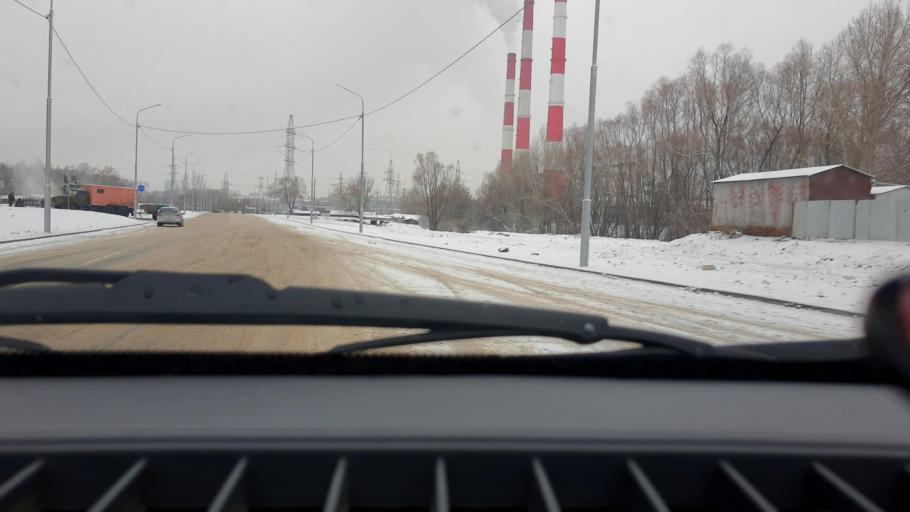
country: RU
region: Bashkortostan
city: Ufa
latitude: 54.7848
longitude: 56.1156
